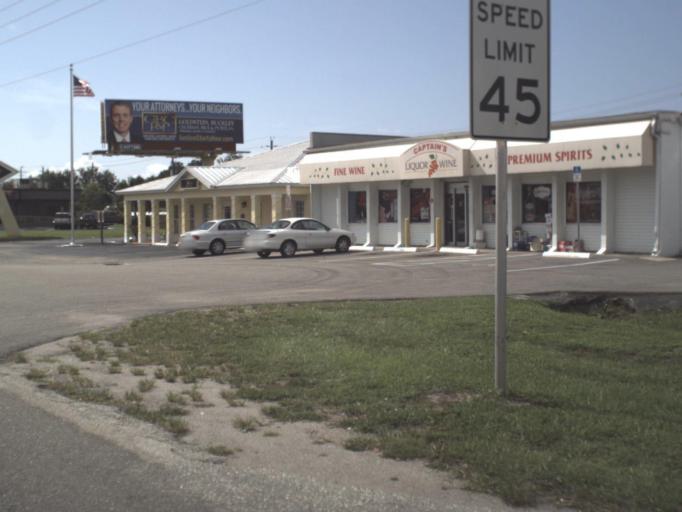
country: US
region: Florida
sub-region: Charlotte County
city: Port Charlotte
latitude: 26.9963
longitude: -82.1186
